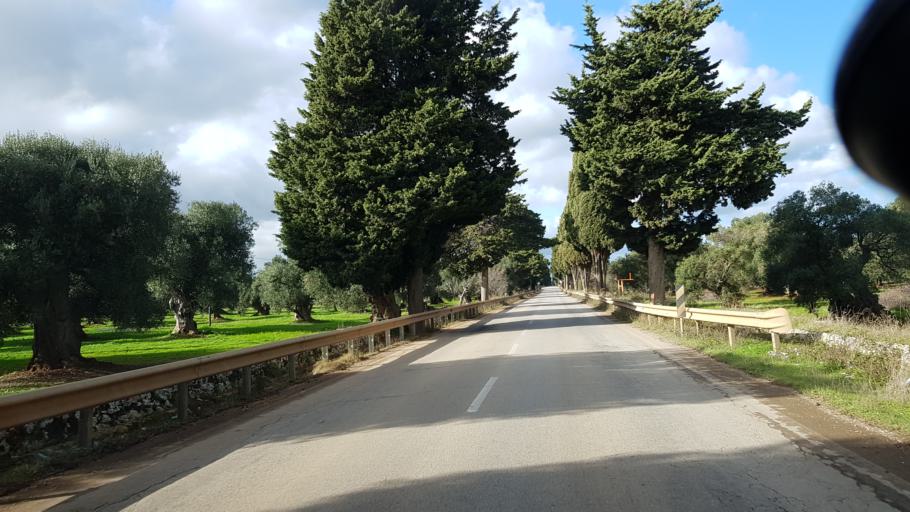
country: IT
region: Apulia
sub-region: Provincia di Brindisi
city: Ostuni
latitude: 40.7558
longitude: 17.5395
